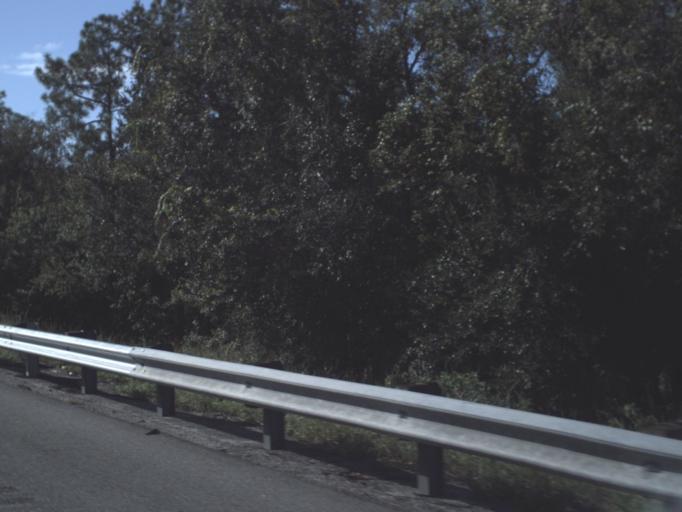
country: US
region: Florida
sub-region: Osceola County
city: Saint Cloud
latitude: 28.2357
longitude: -81.3249
